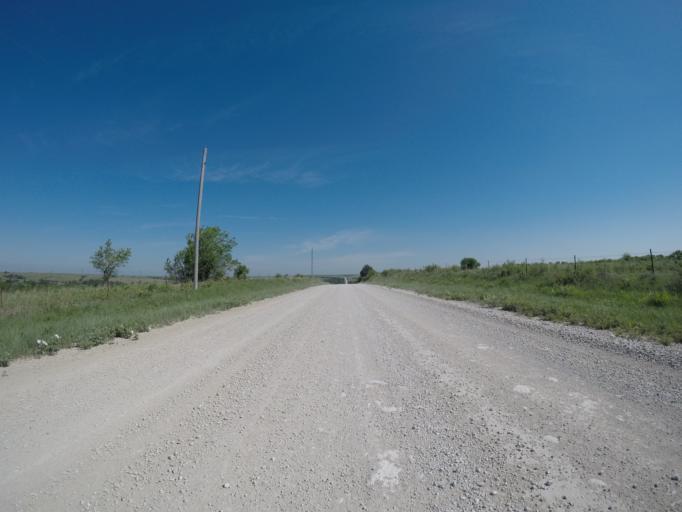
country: US
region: Kansas
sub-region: Wabaunsee County
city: Alma
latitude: 38.9817
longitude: -96.1140
